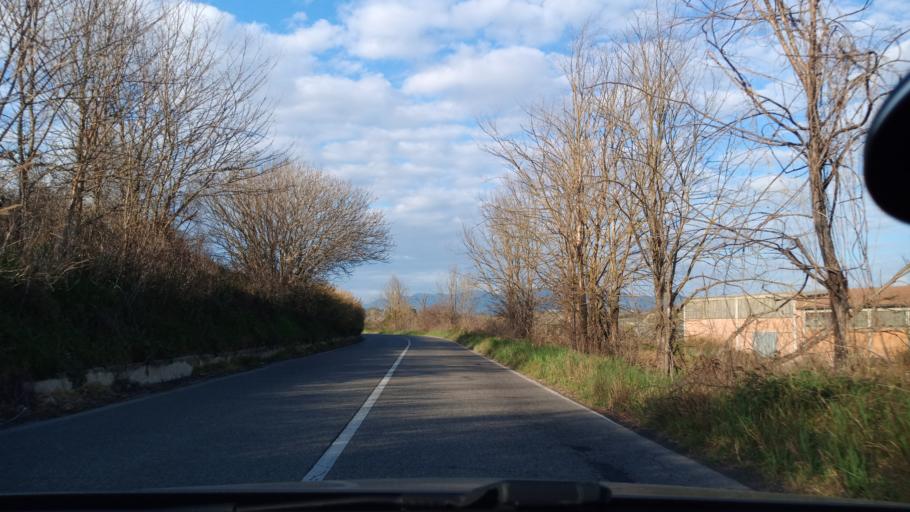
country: IT
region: Latium
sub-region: Citta metropolitana di Roma Capitale
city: Civitella San Paolo
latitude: 42.1955
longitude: 12.6051
